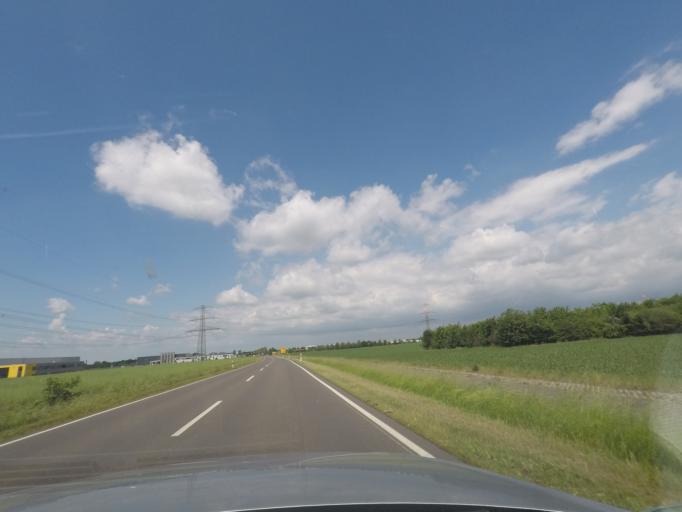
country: DE
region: Saxony
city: Zwenkau
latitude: 51.1999
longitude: 12.3372
